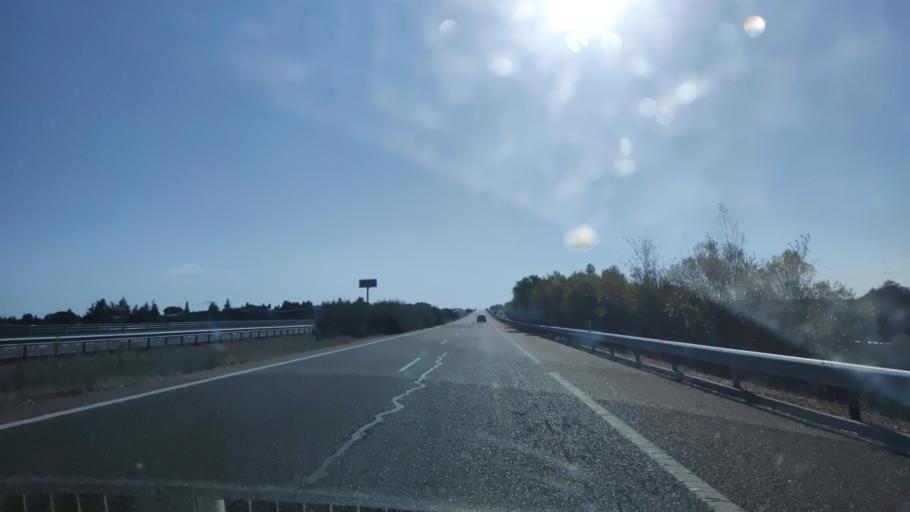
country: ES
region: Castille and Leon
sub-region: Provincia de Salamanca
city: Parada de Arriba
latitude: 40.9322
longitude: -5.8100
